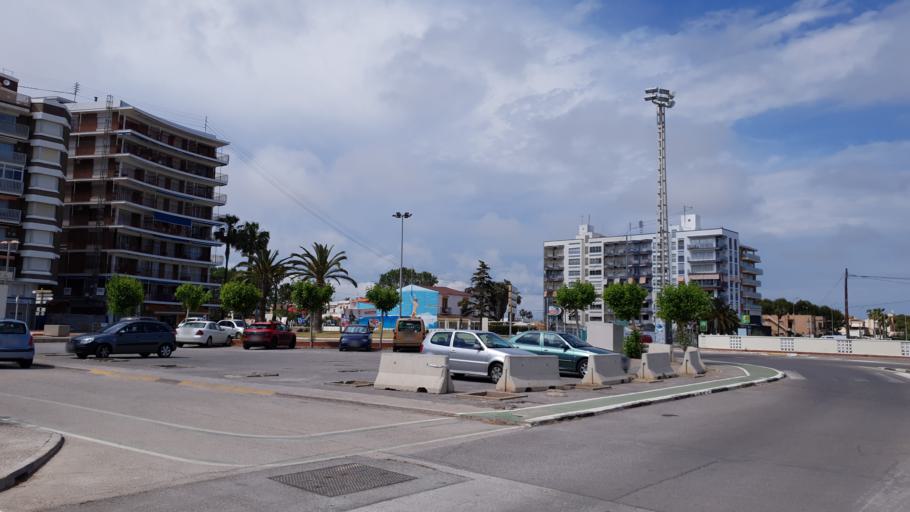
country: ES
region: Valencia
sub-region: Provincia de Castello
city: Burriana
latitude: 39.8652
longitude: -0.0719
